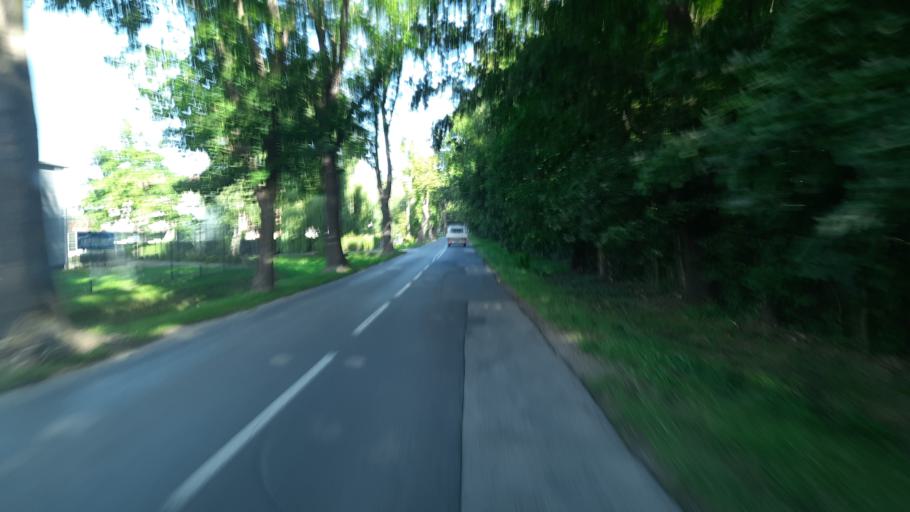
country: PL
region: Lower Silesian Voivodeship
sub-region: Powiat wroclawski
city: Dlugoleka
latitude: 51.1884
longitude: 17.1849
